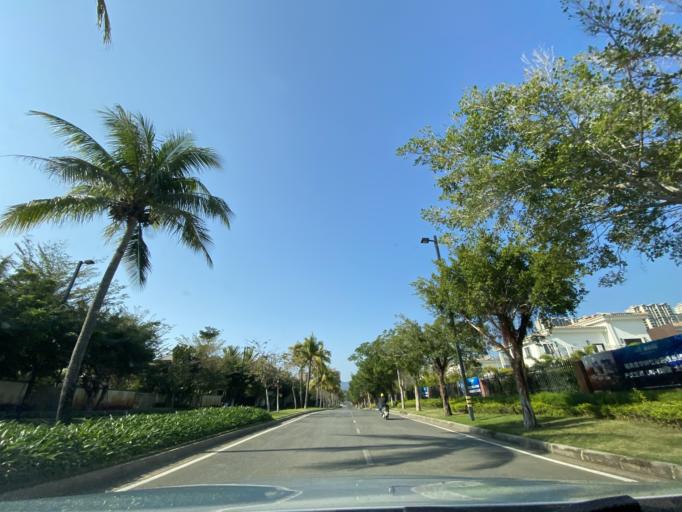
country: CN
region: Hainan
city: Yingzhou
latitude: 18.4153
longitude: 109.8893
